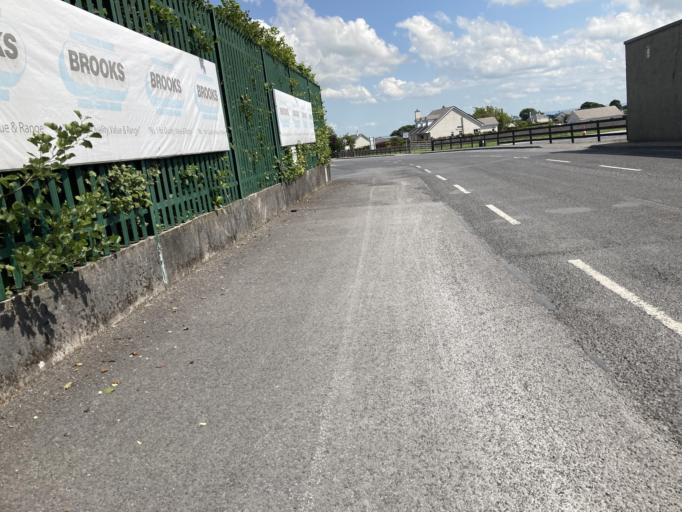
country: IE
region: Connaught
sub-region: County Galway
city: Claregalway
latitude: 53.2978
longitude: -8.9908
